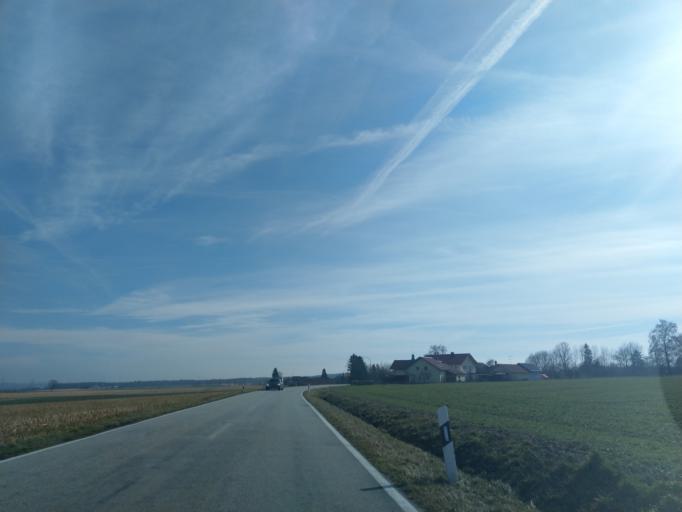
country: DE
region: Bavaria
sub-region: Lower Bavaria
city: Buchhofen
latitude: 48.6636
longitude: 12.9737
